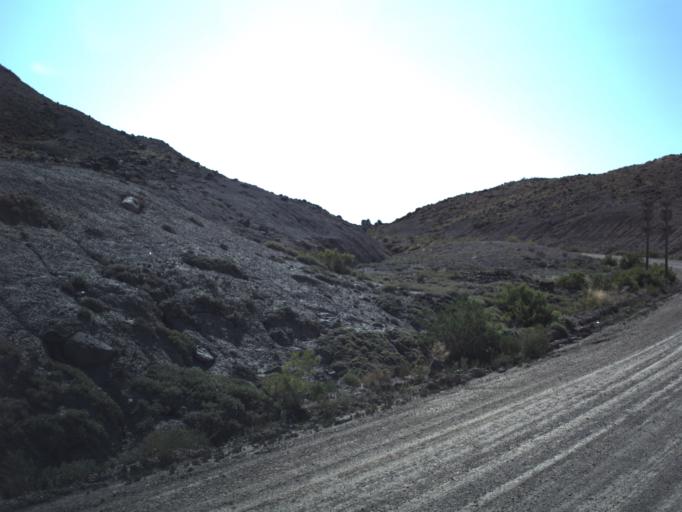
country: US
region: Utah
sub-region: Emery County
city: Ferron
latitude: 38.7638
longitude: -111.3497
